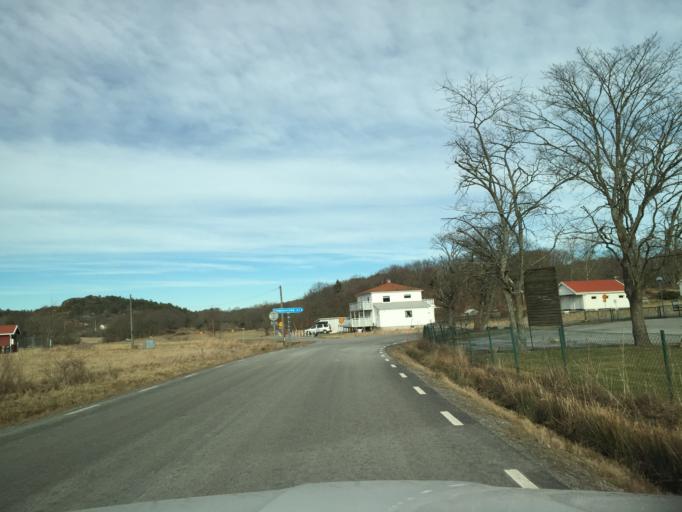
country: SE
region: Vaestra Goetaland
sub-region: Tjorns Kommun
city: Skaerhamn
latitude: 58.0347
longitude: 11.5506
